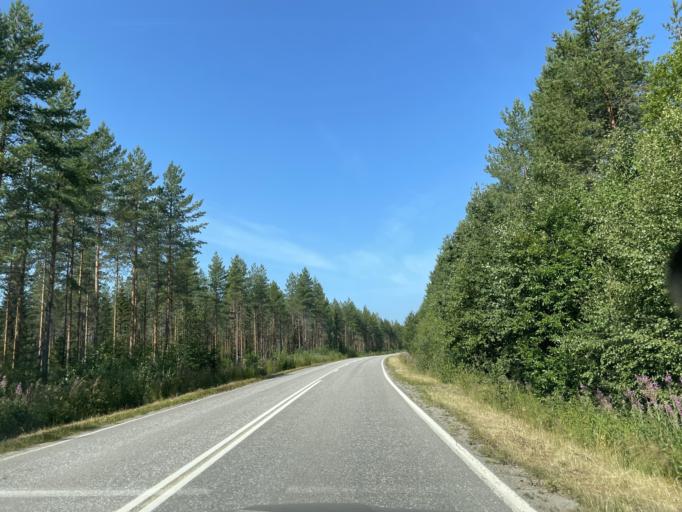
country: FI
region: Central Finland
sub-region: Saarijaervi-Viitasaari
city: Pihtipudas
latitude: 63.3620
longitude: 25.7218
